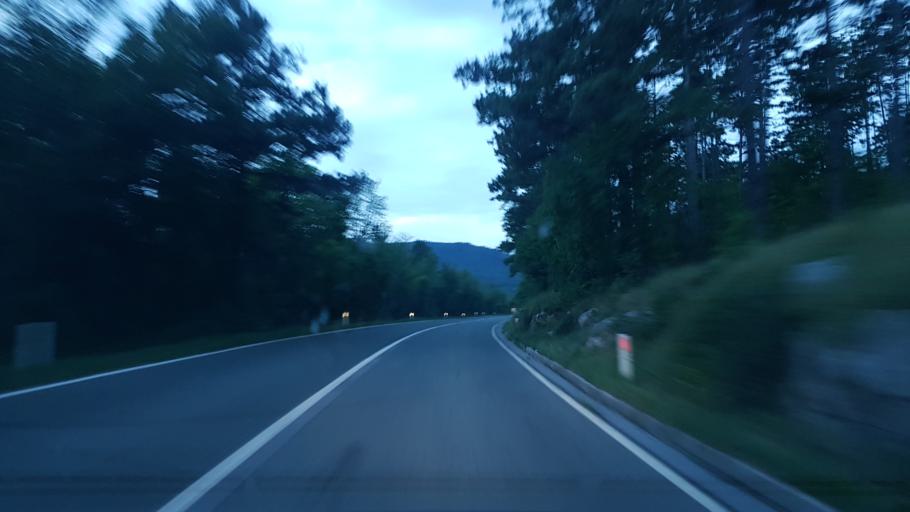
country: SI
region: Divaca
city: Divaca
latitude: 45.6633
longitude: 13.9399
